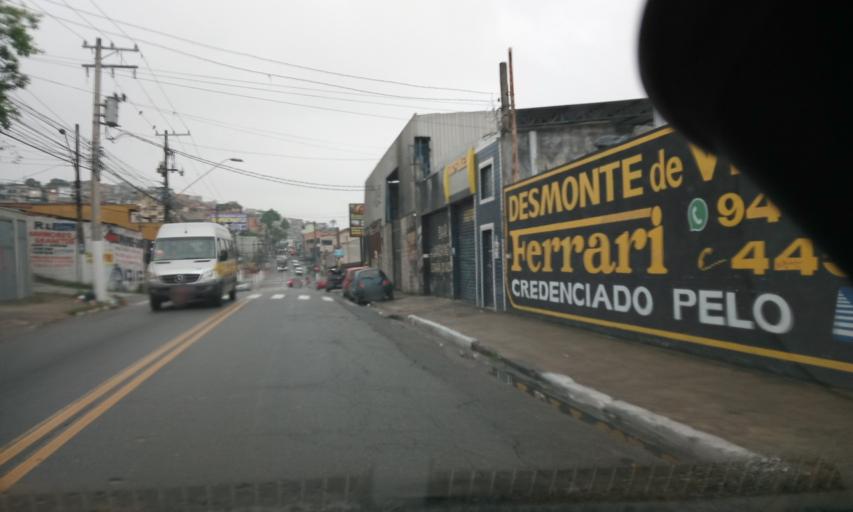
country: BR
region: Sao Paulo
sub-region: Santo Andre
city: Santo Andre
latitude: -23.7011
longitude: -46.5114
